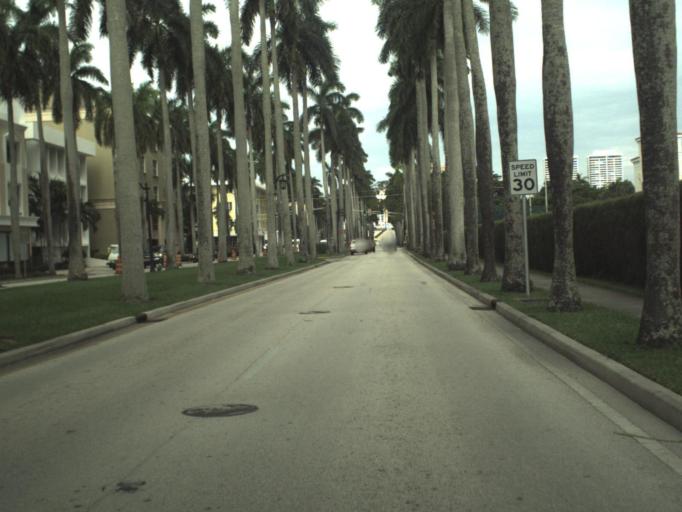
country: US
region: Florida
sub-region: Palm Beach County
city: Palm Beach
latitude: 26.7058
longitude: -80.0393
